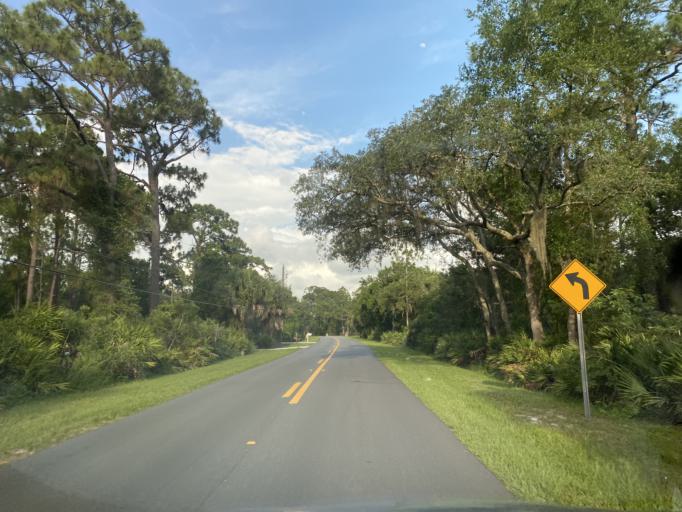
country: US
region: Florida
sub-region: Seminole County
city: Midway
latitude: 28.8458
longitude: -81.1939
